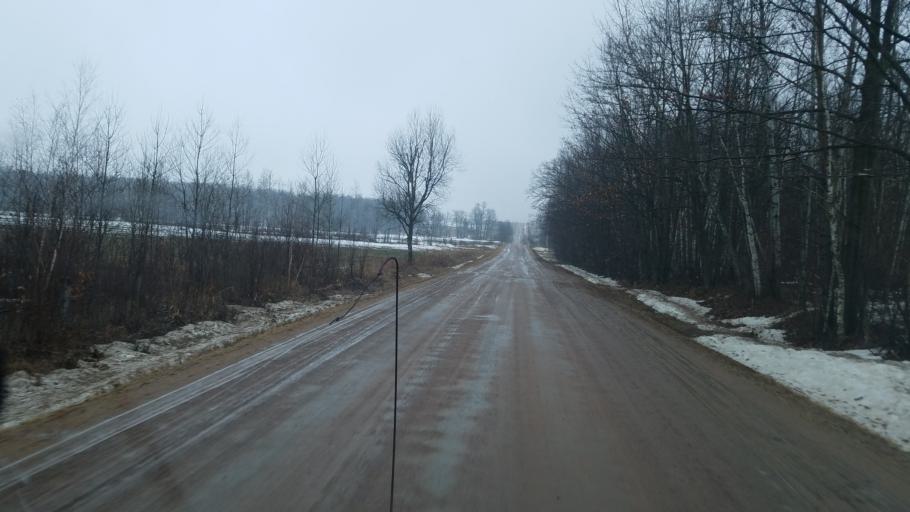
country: US
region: Wisconsin
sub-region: Clark County
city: Loyal
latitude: 44.6083
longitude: -90.3968
